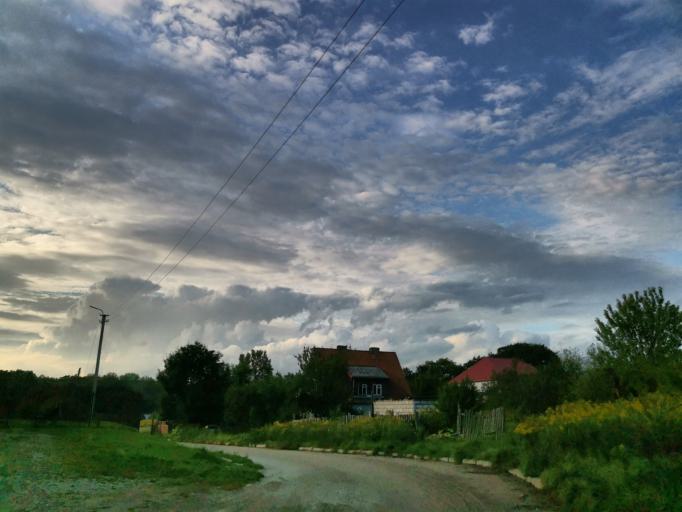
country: RU
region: Kaliningrad
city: Chernyakhovsk
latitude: 54.6511
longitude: 21.8168
